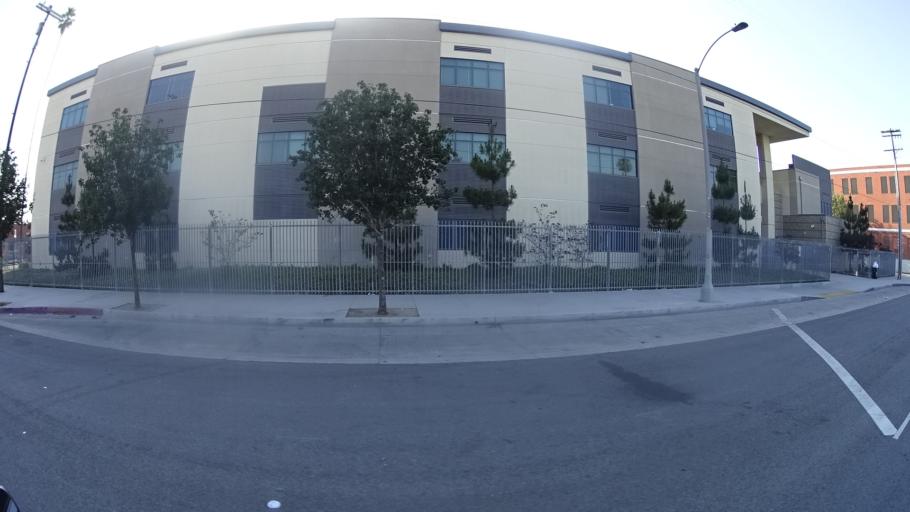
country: US
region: California
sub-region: Los Angeles County
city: Westmont
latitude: 33.9777
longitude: -118.2916
